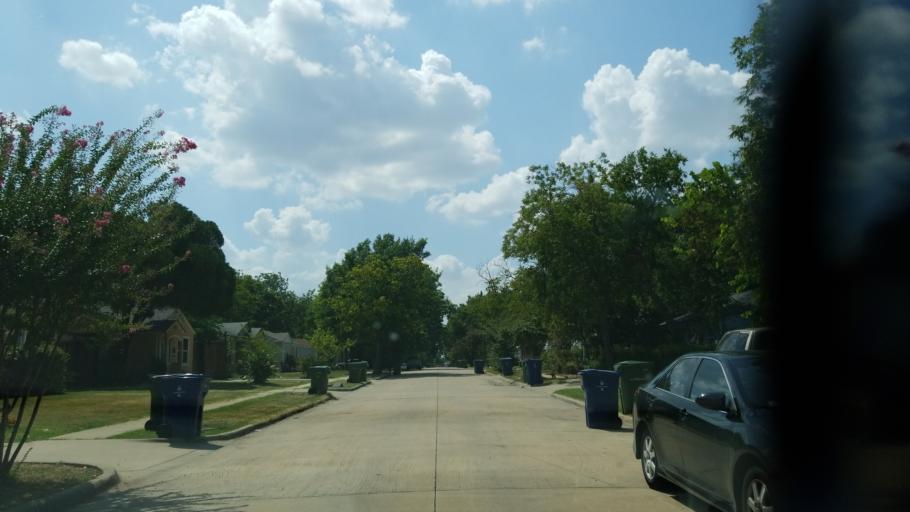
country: US
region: Texas
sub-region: Dallas County
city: Garland
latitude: 32.9189
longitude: -96.6451
